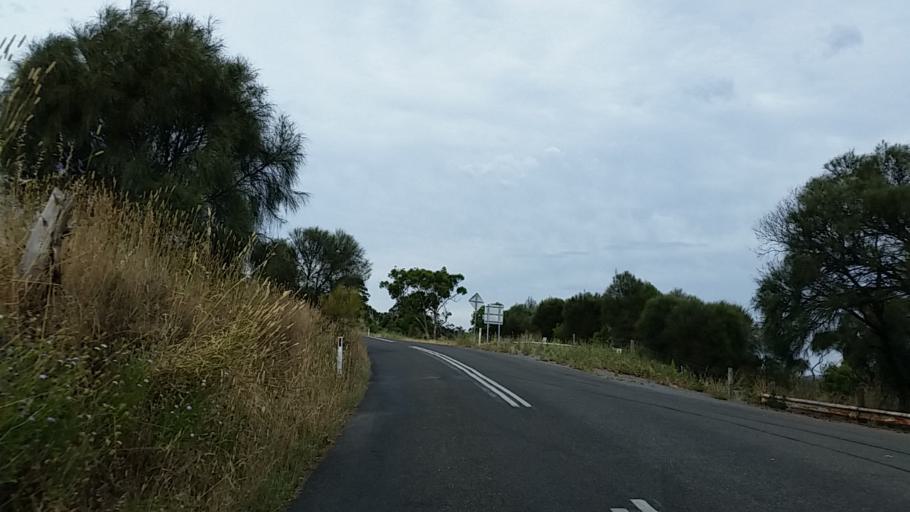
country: AU
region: South Australia
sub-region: Yankalilla
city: Normanville
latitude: -35.3995
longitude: 138.4180
